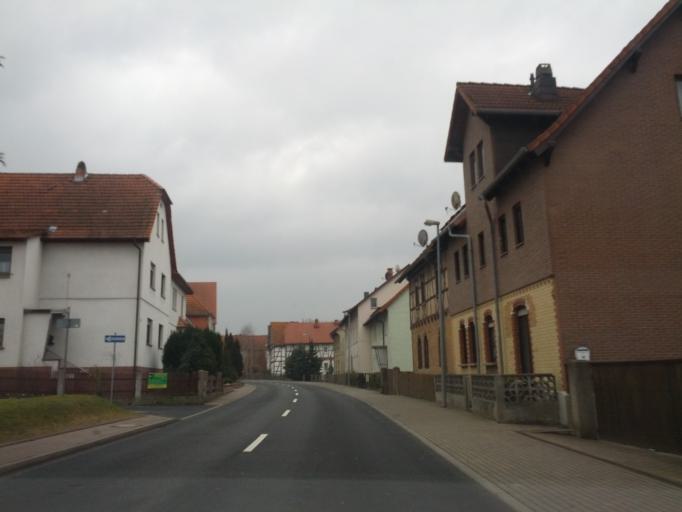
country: DE
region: Thuringia
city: Dippach
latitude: 50.9232
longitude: 10.0450
